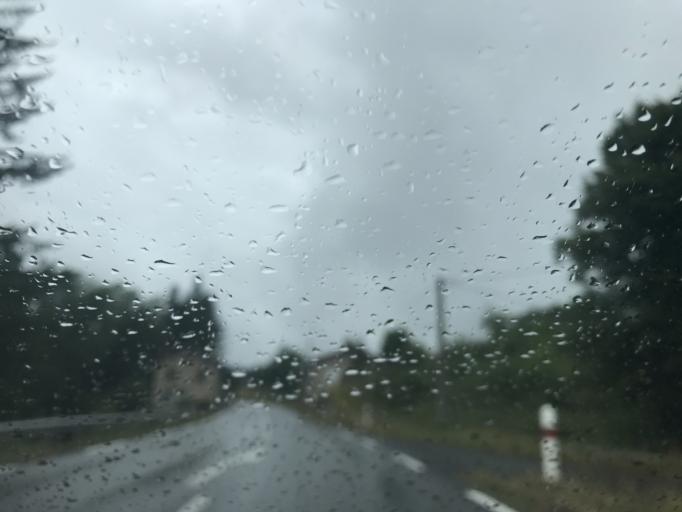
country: FR
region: Auvergne
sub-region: Departement du Puy-de-Dome
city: Job
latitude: 45.6263
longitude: 3.7156
